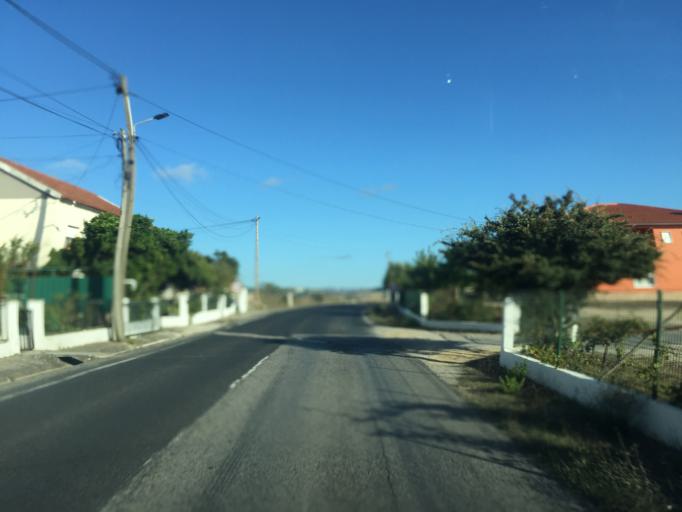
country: PT
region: Lisbon
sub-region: Torres Vedras
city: Torres Vedras
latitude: 39.1164
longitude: -9.2623
